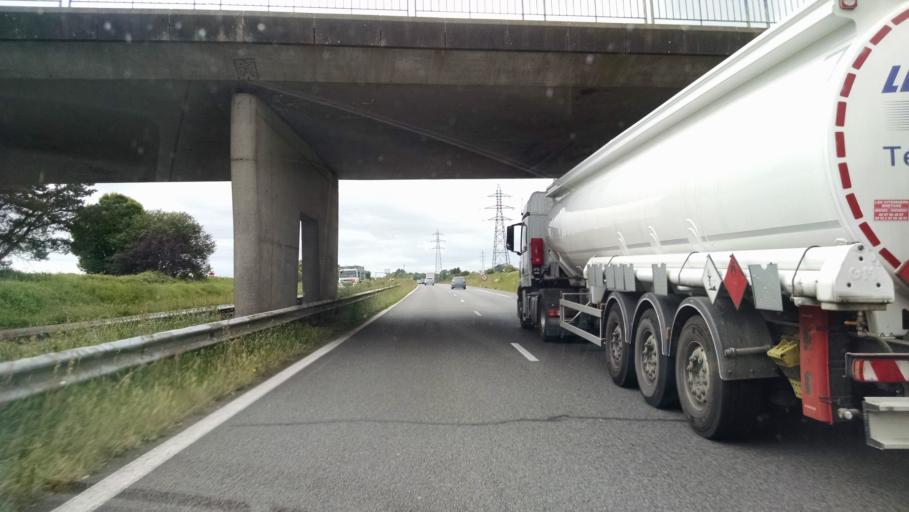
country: FR
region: Brittany
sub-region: Departement du Finistere
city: Bannalec
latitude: 47.8868
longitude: -3.7000
